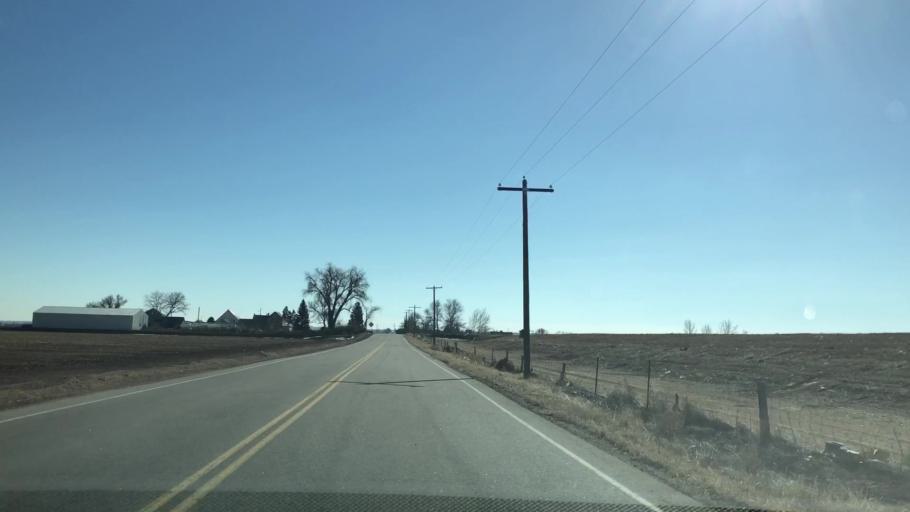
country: US
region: Colorado
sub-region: Weld County
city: Windsor
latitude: 40.5124
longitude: -104.9443
